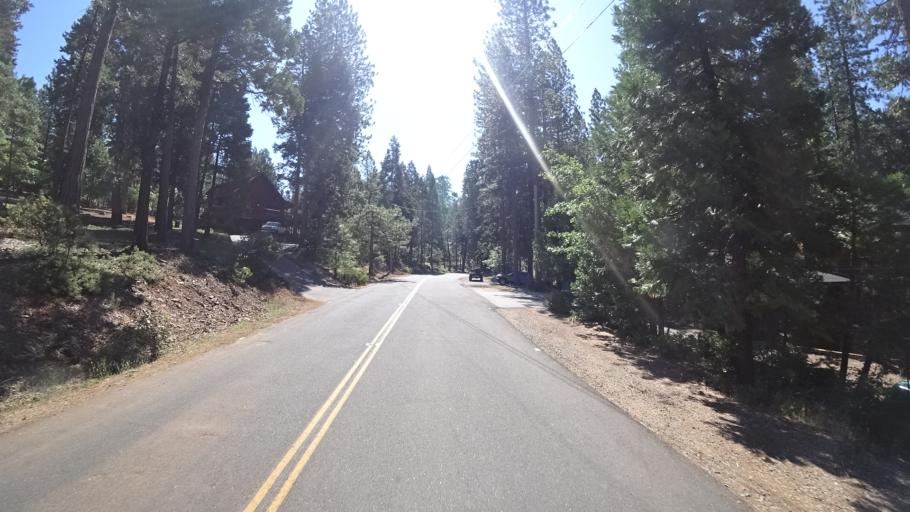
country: US
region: California
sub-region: Calaveras County
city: Arnold
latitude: 38.2489
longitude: -120.3718
